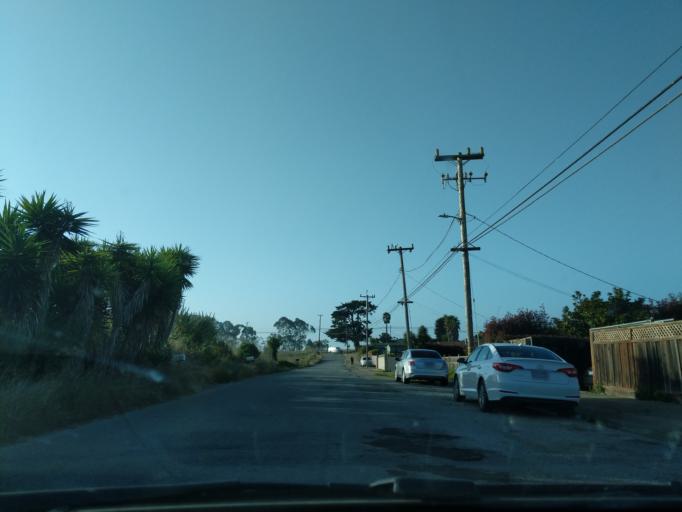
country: US
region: California
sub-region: Monterey County
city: Las Lomas
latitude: 36.8709
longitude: -121.7626
